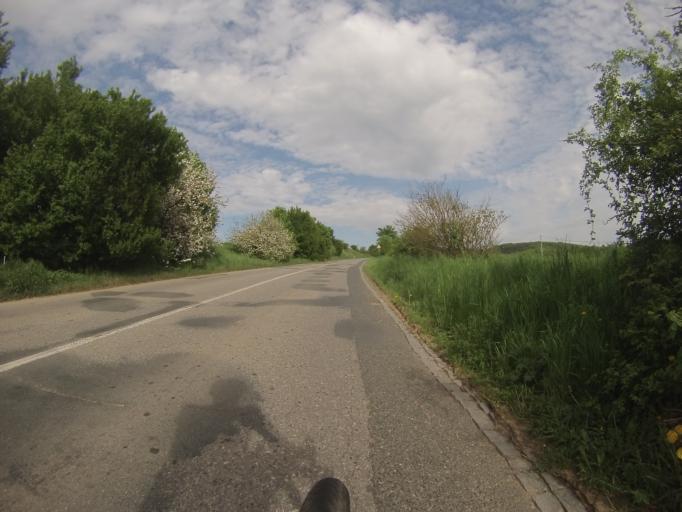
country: CZ
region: South Moravian
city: Veverska Bityska
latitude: 49.2531
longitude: 16.4508
